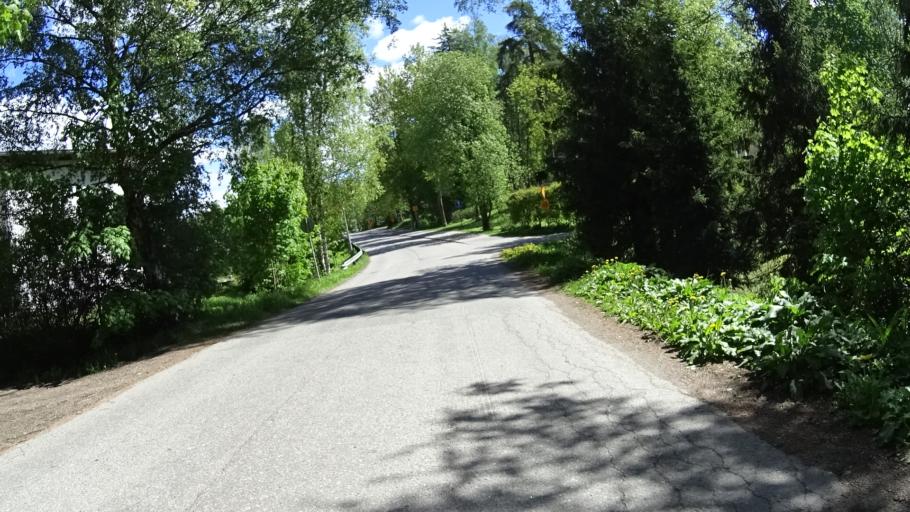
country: FI
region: Uusimaa
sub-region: Helsinki
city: Kauniainen
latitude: 60.2231
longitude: 24.7065
